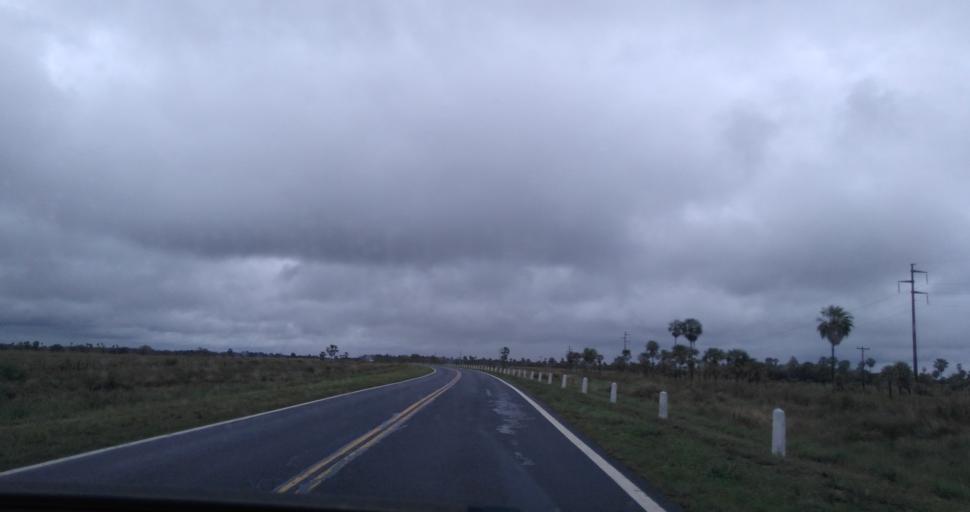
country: AR
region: Formosa
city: Clorinda
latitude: -25.6319
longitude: -57.9188
